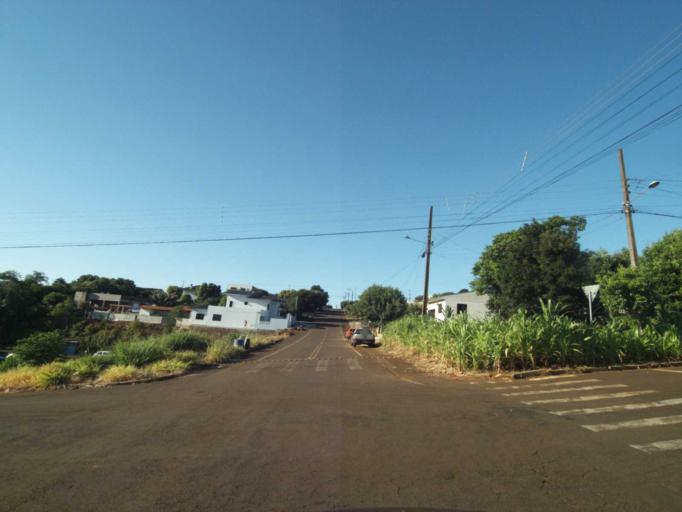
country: BR
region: Parana
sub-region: Coronel Vivida
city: Coronel Vivida
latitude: -25.9606
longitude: -52.8131
